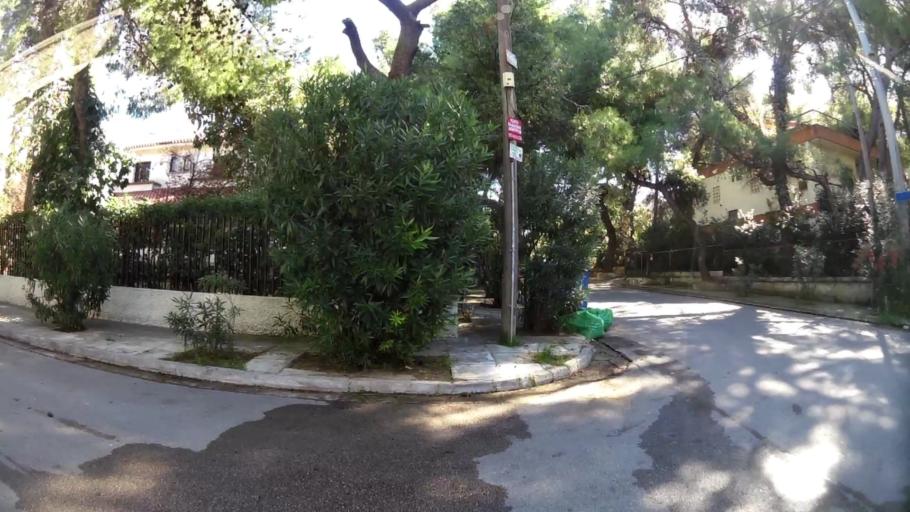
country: GR
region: Attica
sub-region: Nomarchia Athinas
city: Nea Erythraia
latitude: 38.0956
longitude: 23.8058
